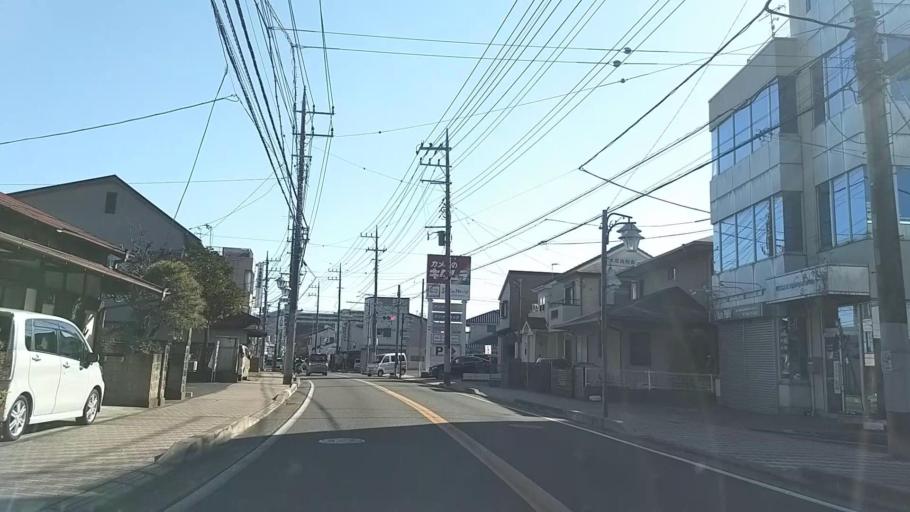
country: JP
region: Kanagawa
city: Hadano
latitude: 35.3781
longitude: 139.2223
